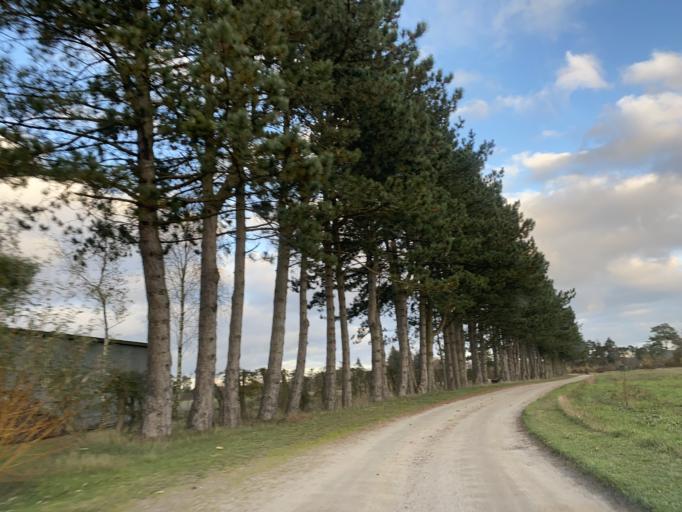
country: DK
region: Central Jutland
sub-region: Silkeborg Kommune
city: Svejbaek
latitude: 56.1811
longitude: 9.6260
